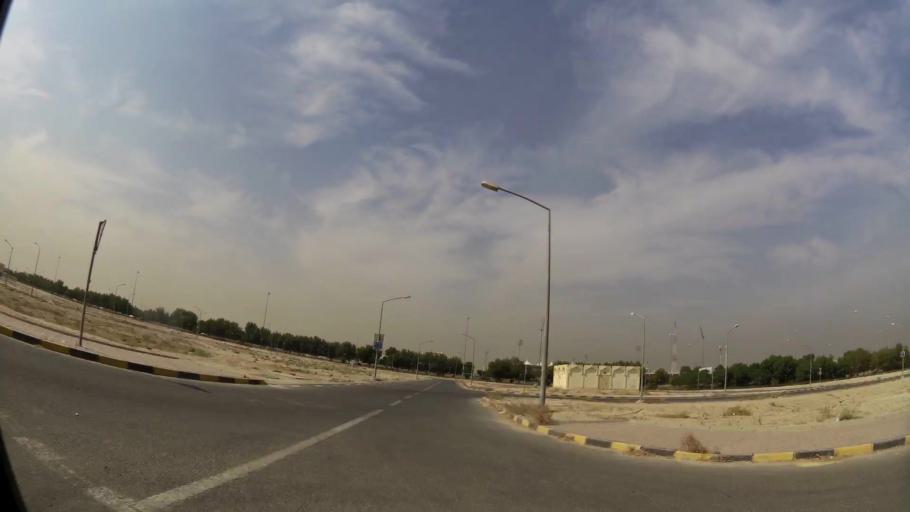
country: KW
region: Al Farwaniyah
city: Janub as Surrah
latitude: 29.2816
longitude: 47.9883
